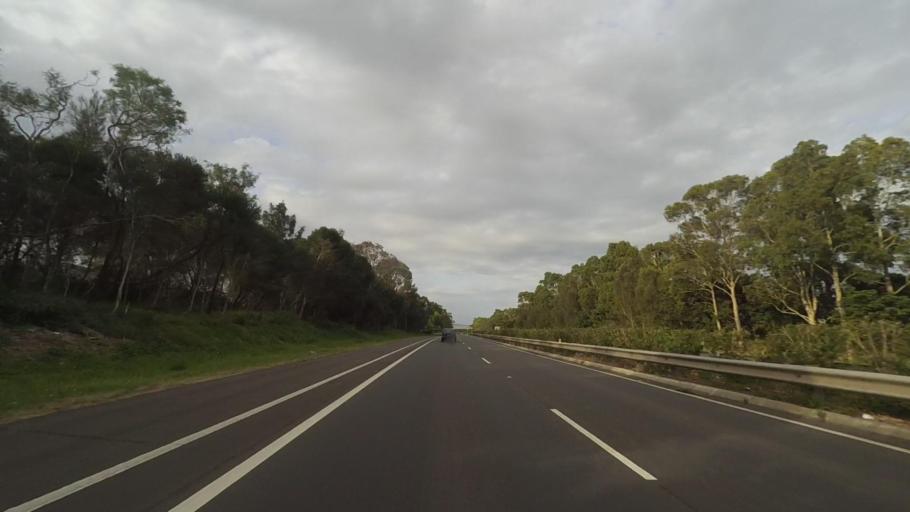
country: AU
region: New South Wales
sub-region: Wollongong
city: Fairy Meadow
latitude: -34.3998
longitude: 150.8937
